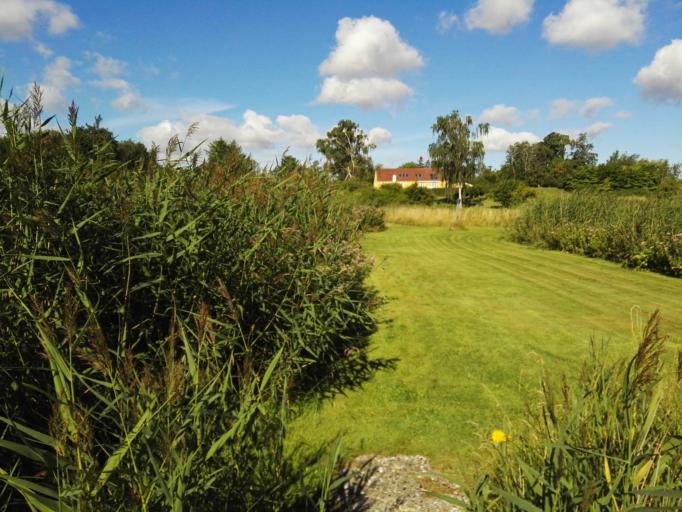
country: DK
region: Capital Region
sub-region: Frederikssund Kommune
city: Frederikssund
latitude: 55.7909
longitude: 12.0565
